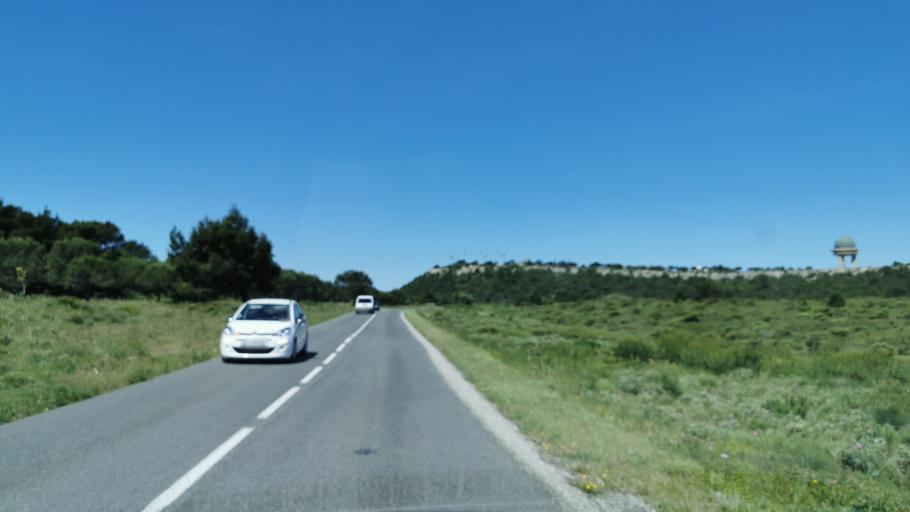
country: FR
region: Languedoc-Roussillon
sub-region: Departement de l'Aude
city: Armissan
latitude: 43.1694
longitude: 3.1286
